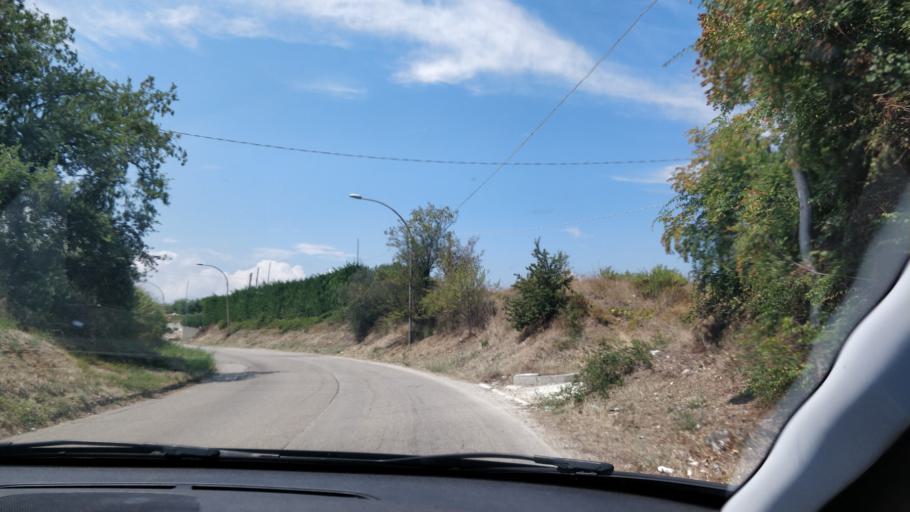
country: IT
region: Abruzzo
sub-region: Provincia di Chieti
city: Francavilla al Mare
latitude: 42.4242
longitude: 14.2574
